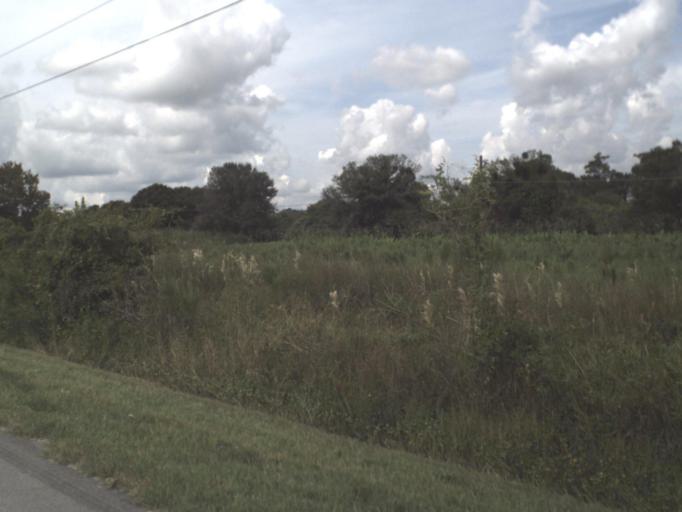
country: US
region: Florida
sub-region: Okeechobee County
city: Taylor Creek
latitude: 27.2547
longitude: -80.7668
